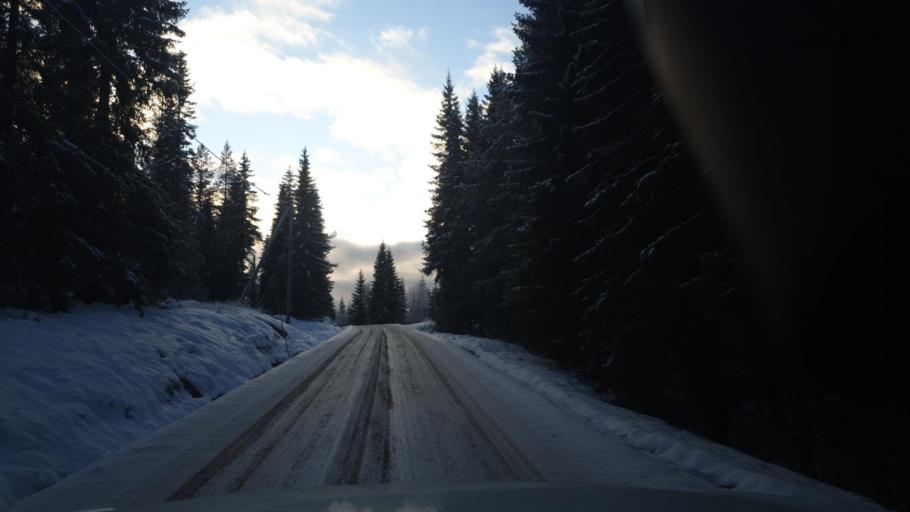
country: SE
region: Vaermland
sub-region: Eda Kommun
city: Charlottenberg
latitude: 60.1368
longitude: 12.5937
